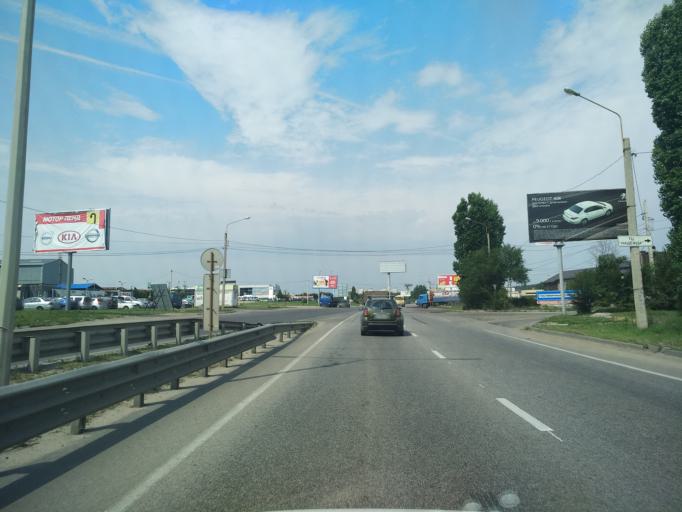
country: RU
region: Voronezj
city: Somovo
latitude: 51.6785
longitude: 39.2940
